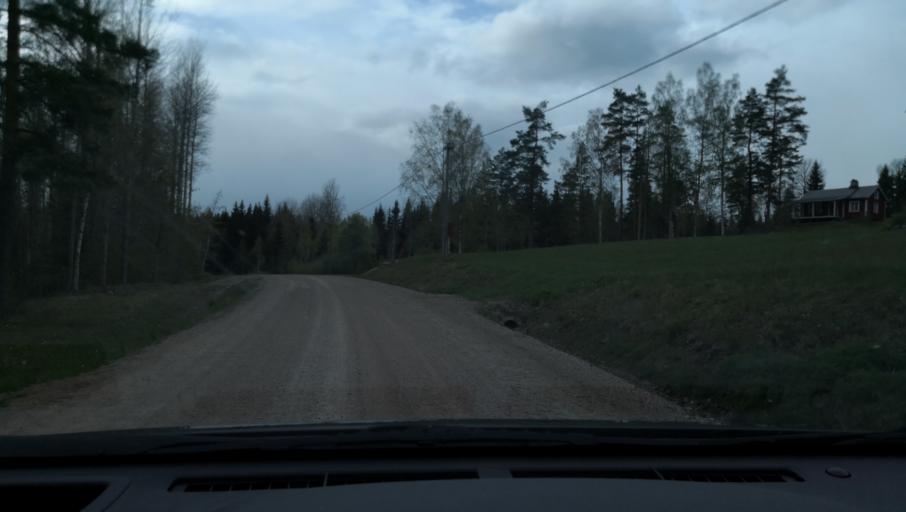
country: SE
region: Vaestmanland
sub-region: Fagersta Kommun
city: Fagersta
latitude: 60.1220
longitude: 15.7432
